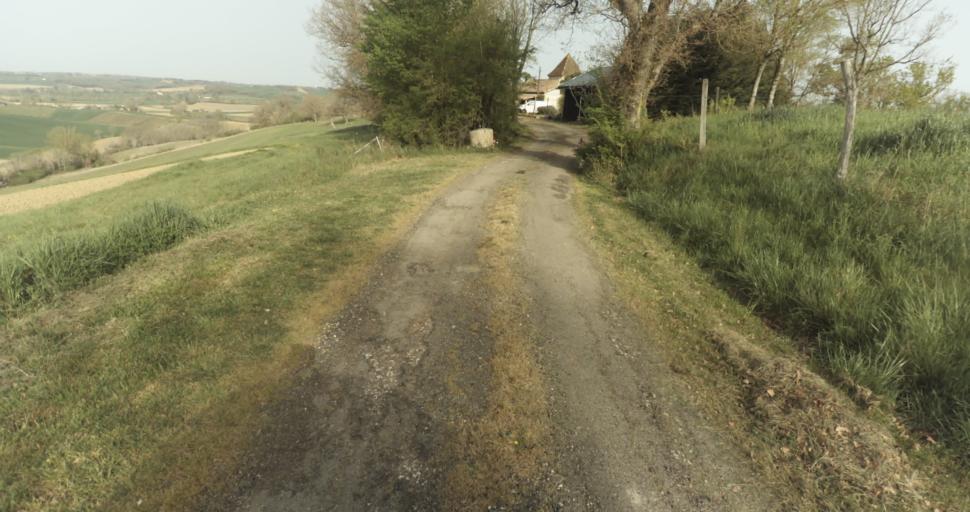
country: FR
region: Midi-Pyrenees
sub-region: Departement du Tarn-et-Garonne
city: Saint-Nicolas-de-la-Grave
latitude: 44.1593
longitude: 1.0179
